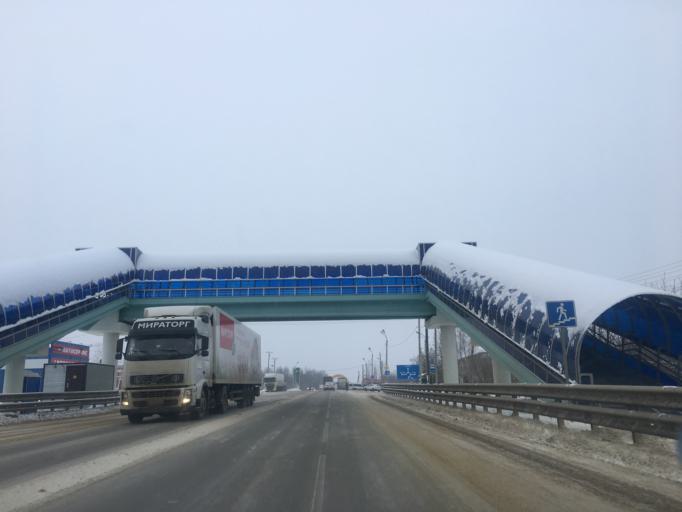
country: RU
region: Tula
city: Kosaya Gora
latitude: 54.1627
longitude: 37.4705
